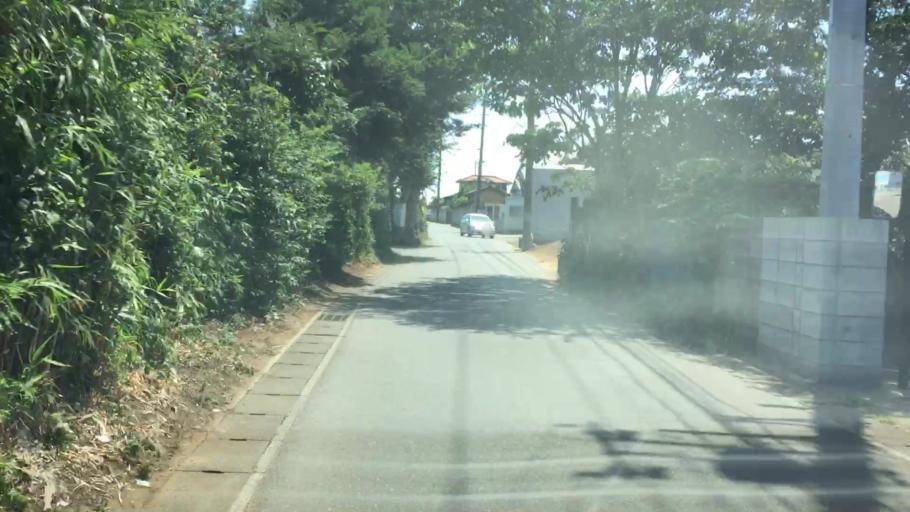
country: JP
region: Chiba
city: Matsudo
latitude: 35.7624
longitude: 139.9356
